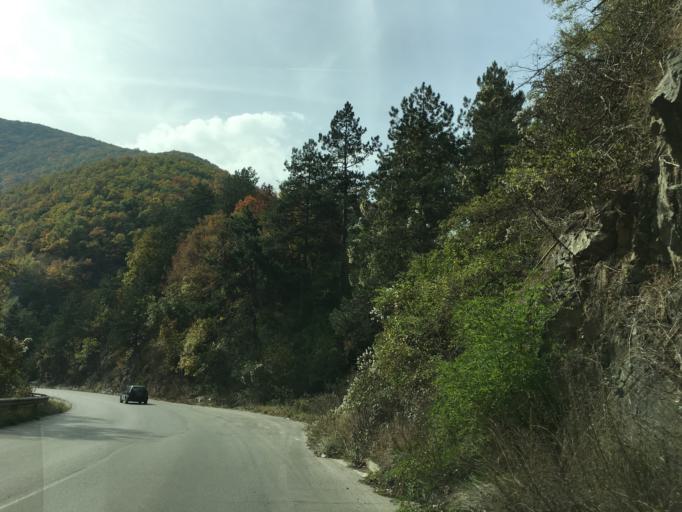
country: BG
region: Sofia-Capital
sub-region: Stolichna Obshtina
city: Sofia
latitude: 42.5615
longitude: 23.4233
